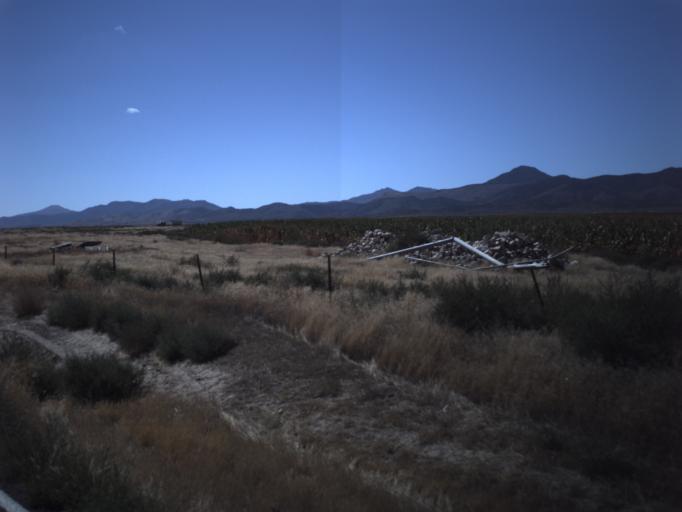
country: US
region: Utah
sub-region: Utah County
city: Genola
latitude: 40.0689
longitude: -111.9586
